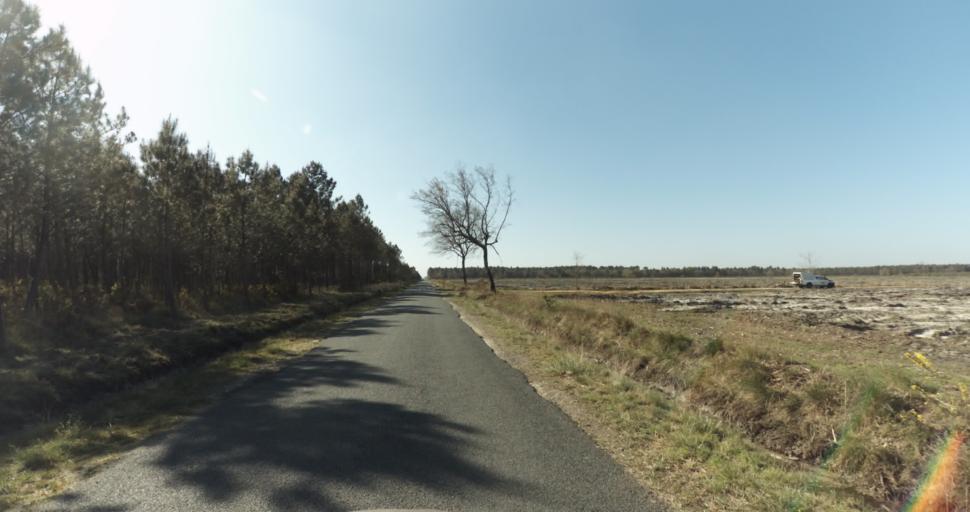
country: FR
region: Aquitaine
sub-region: Departement de la Gironde
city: Martignas-sur-Jalle
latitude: 44.7921
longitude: -0.8646
